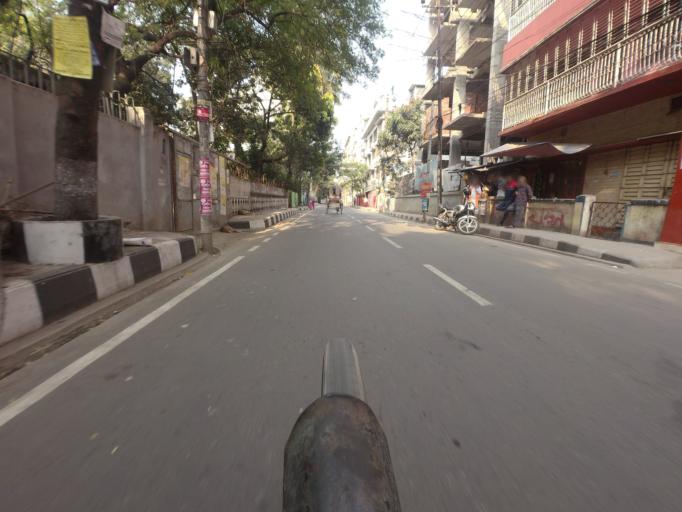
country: BD
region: Dhaka
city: Azimpur
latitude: 23.7628
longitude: 90.3685
